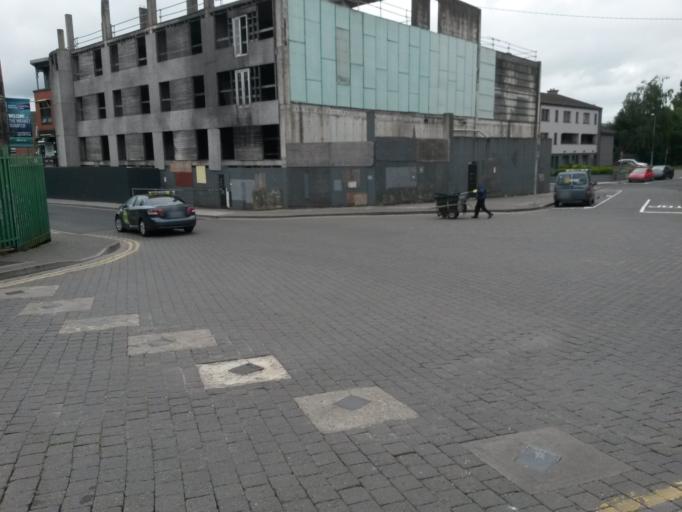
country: IE
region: Munster
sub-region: County Limerick
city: Luimneach
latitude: 52.6640
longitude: -8.6222
